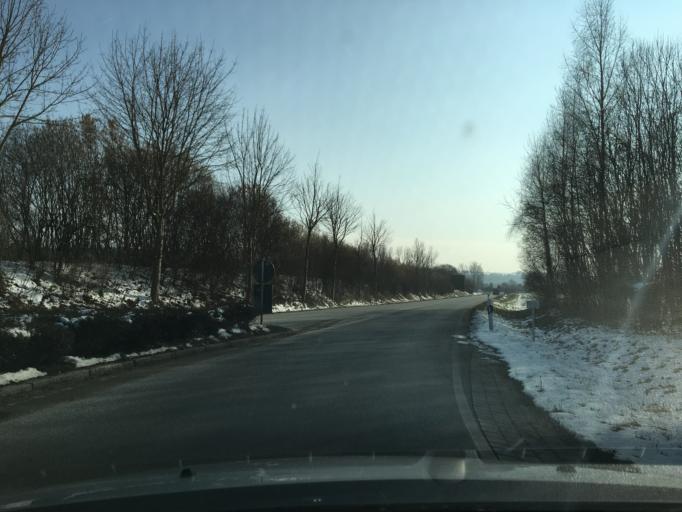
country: DE
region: Bavaria
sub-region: Lower Bavaria
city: Gottfrieding
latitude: 48.6503
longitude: 12.5242
